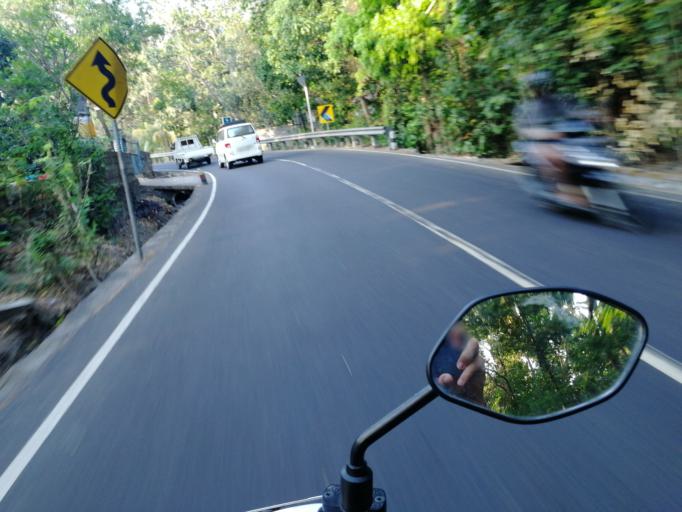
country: ID
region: Bali
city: Banjar Kangkaang
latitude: -8.3527
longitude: 115.6134
